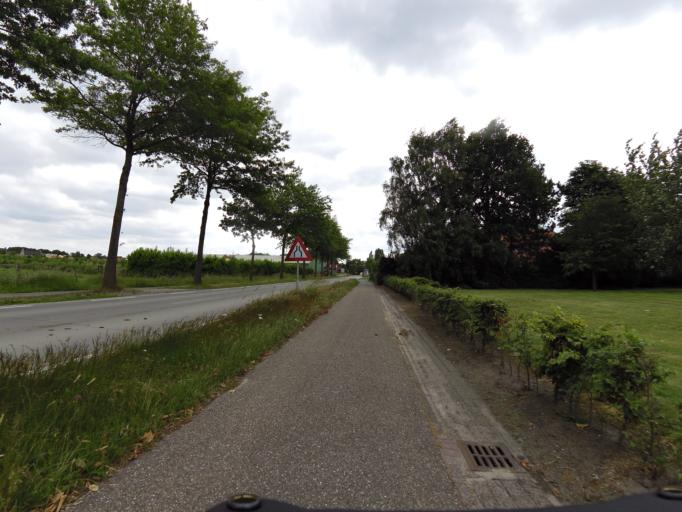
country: NL
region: North Brabant
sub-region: Gemeente Baarle-Nassau
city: Baarle-Nassau
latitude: 51.4457
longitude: 4.9119
